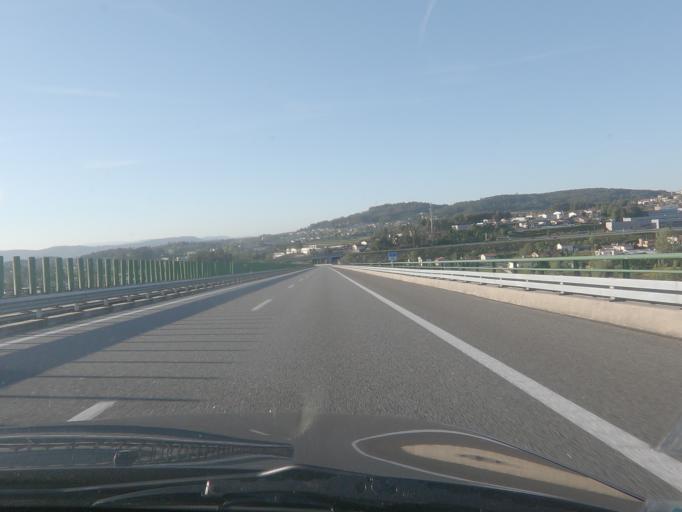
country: PT
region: Braga
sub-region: Braga
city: Oliveira
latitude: 41.5260
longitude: -8.4835
